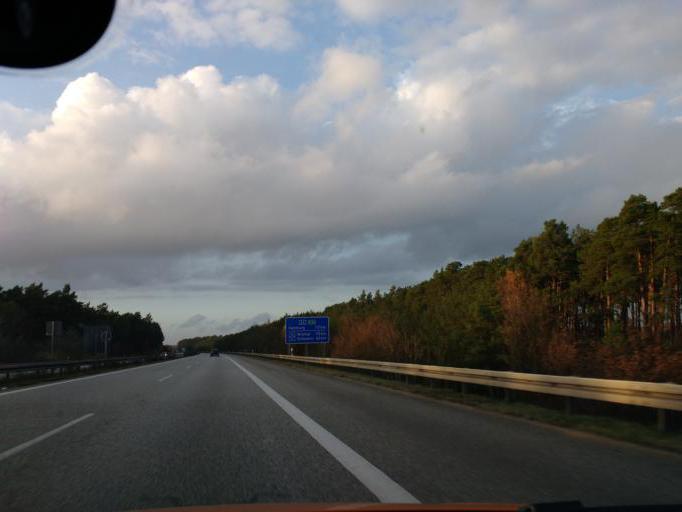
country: DE
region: Mecklenburg-Vorpommern
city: Neustadt-Glewe
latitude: 53.3853
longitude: 11.6136
